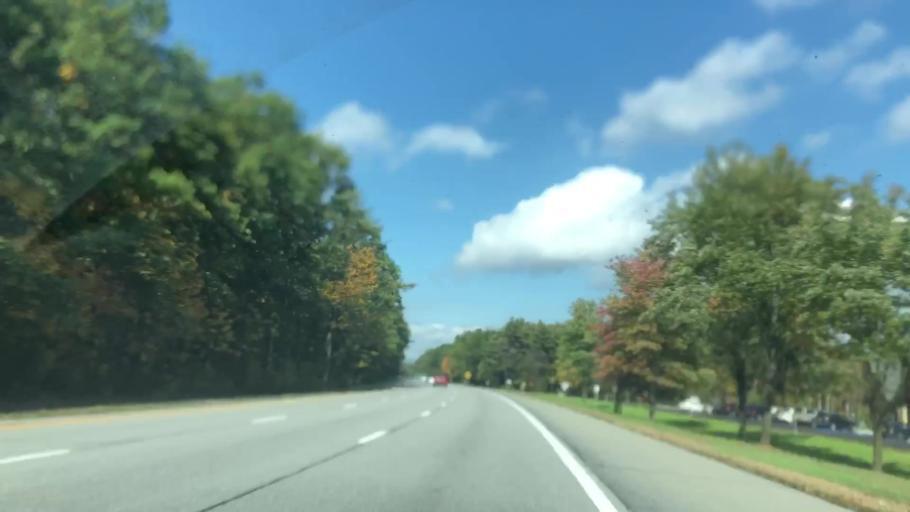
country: US
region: New York
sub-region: Warren County
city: West Glens Falls
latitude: 43.2721
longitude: -73.6745
